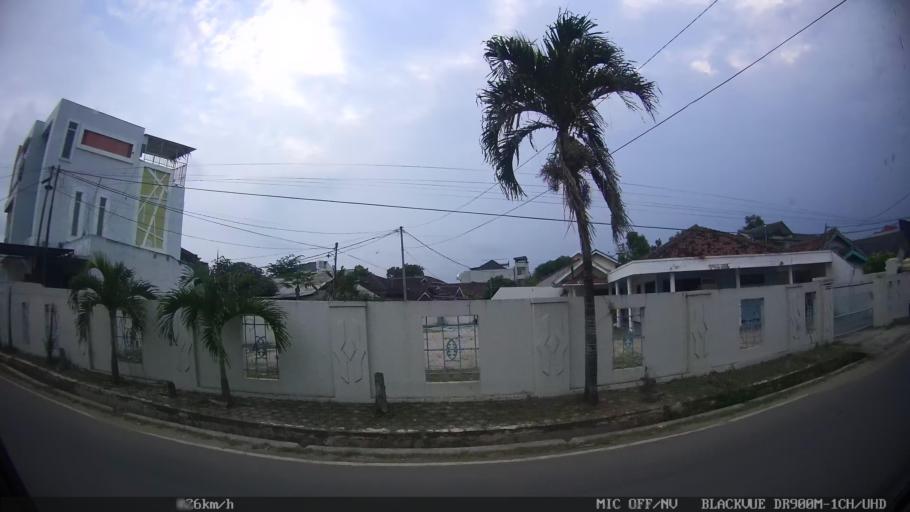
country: ID
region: Lampung
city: Kedaton
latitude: -5.4037
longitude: 105.2845
